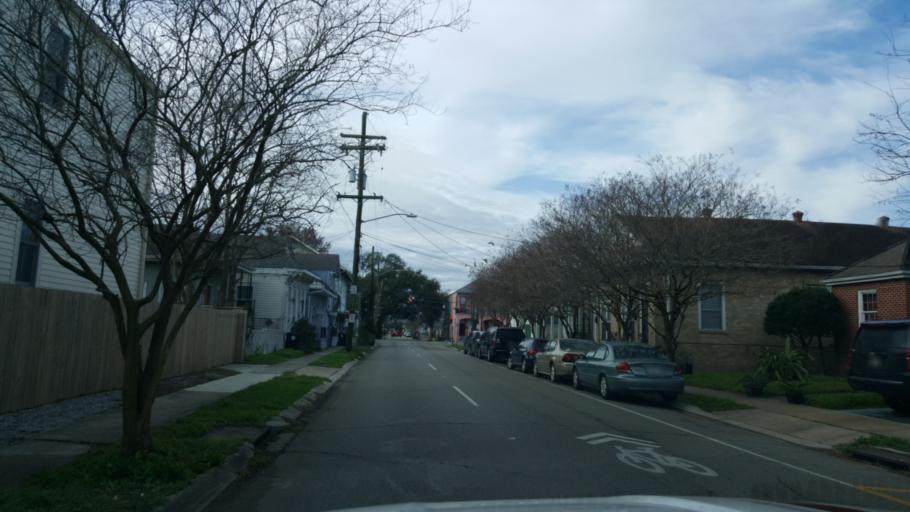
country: US
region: Louisiana
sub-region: Orleans Parish
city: New Orleans
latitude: 29.9717
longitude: -90.0751
